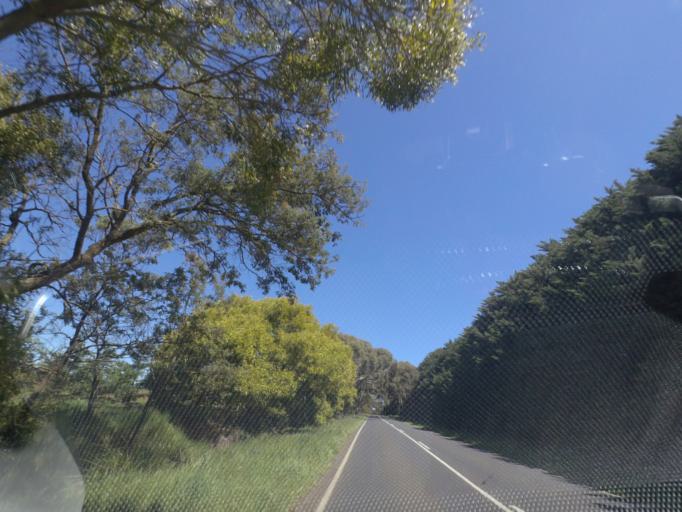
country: AU
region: Victoria
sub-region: Hume
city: Sunbury
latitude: -37.3139
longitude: 144.6671
